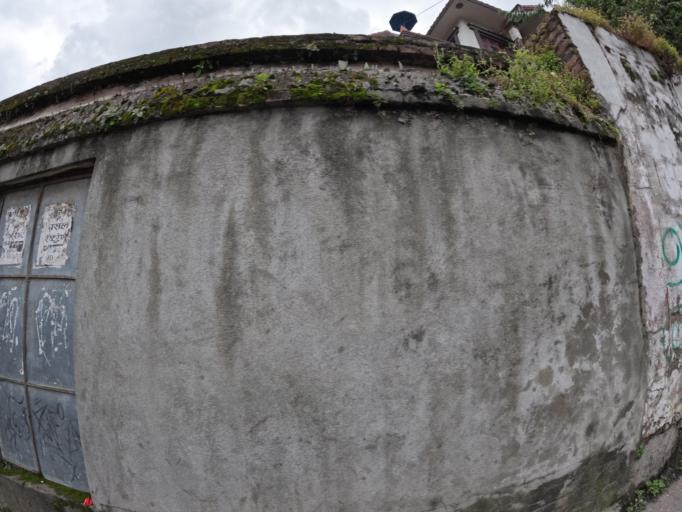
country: NP
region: Central Region
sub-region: Bagmati Zone
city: Kathmandu
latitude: 27.7381
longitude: 85.3130
